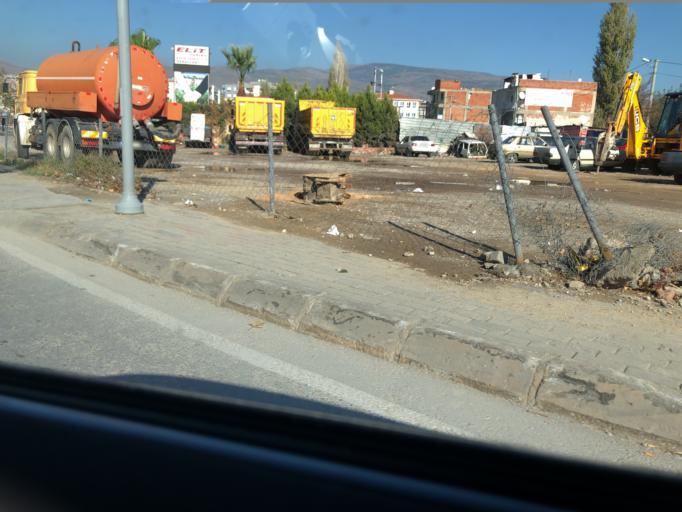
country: TR
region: Izmir
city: Izmir
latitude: 38.4553
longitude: 27.1772
